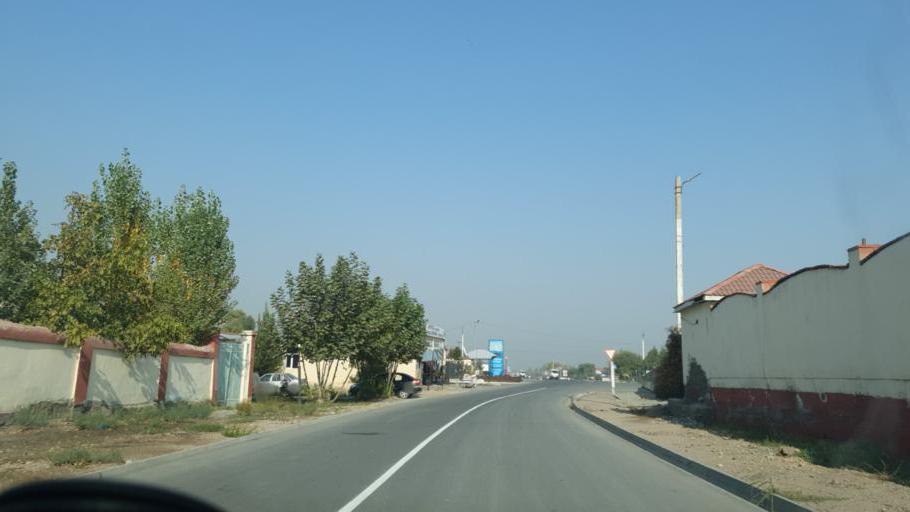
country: UZ
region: Fergana
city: Qo`qon
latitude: 40.5873
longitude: 70.9052
